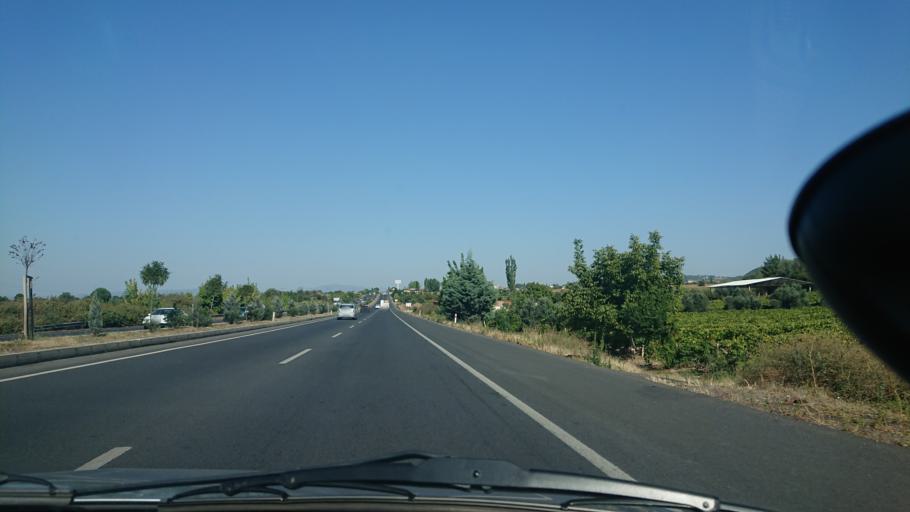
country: TR
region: Manisa
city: Ahmetli
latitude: 38.4939
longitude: 27.8532
